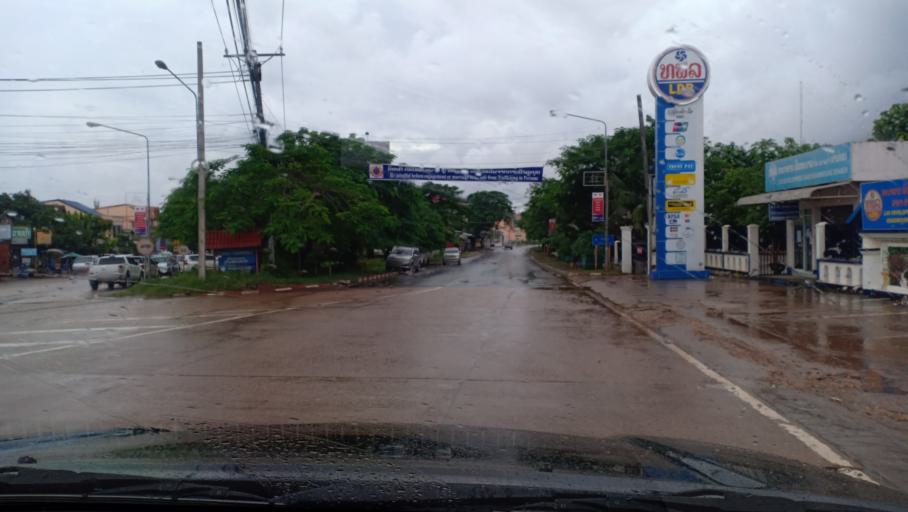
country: LA
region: Khammouan
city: Thakhek
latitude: 17.4009
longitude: 104.8211
